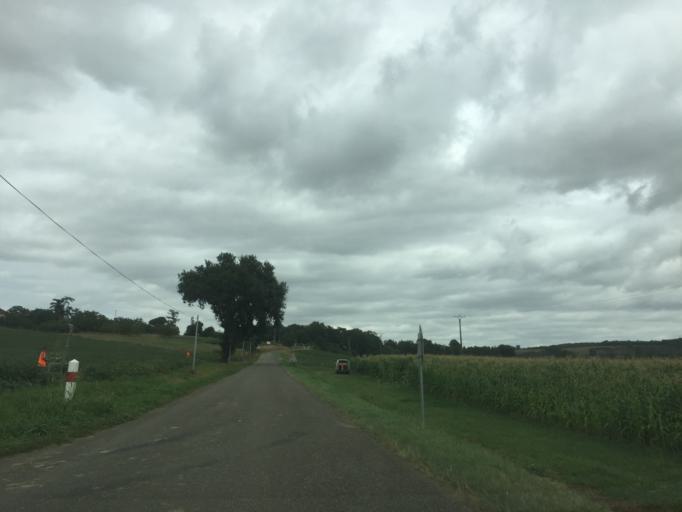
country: FR
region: Midi-Pyrenees
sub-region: Departement du Gers
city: Mirande
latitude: 43.6109
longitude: 0.3406
